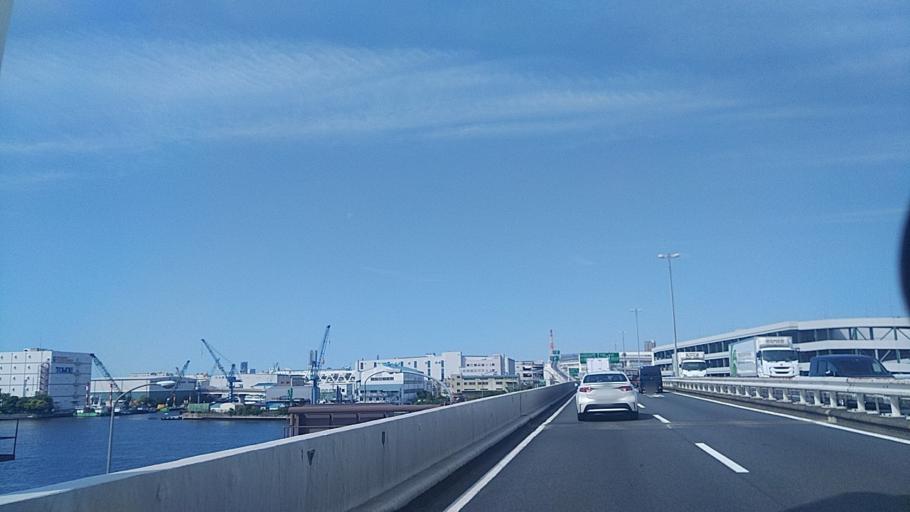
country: JP
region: Kanagawa
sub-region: Kawasaki-shi
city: Kawasaki
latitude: 35.4950
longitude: 139.6789
